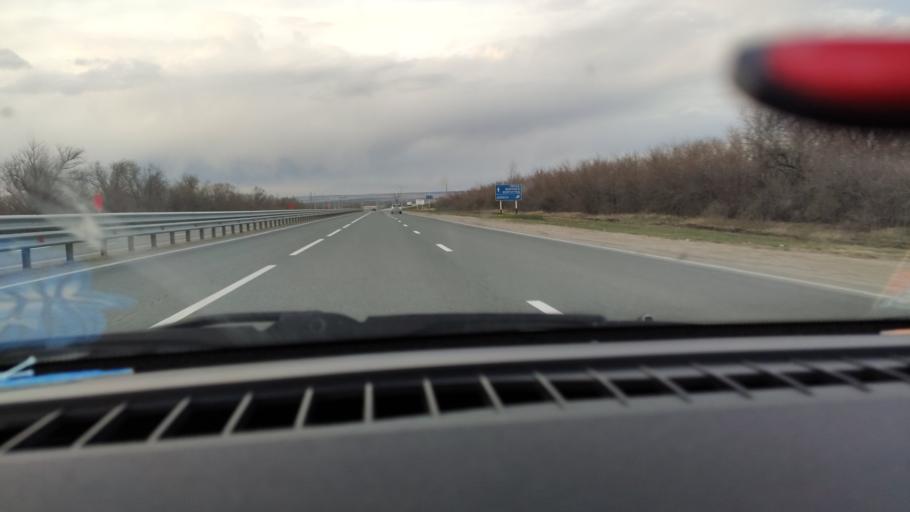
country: RU
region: Saratov
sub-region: Saratovskiy Rayon
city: Saratov
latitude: 51.6659
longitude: 46.0002
